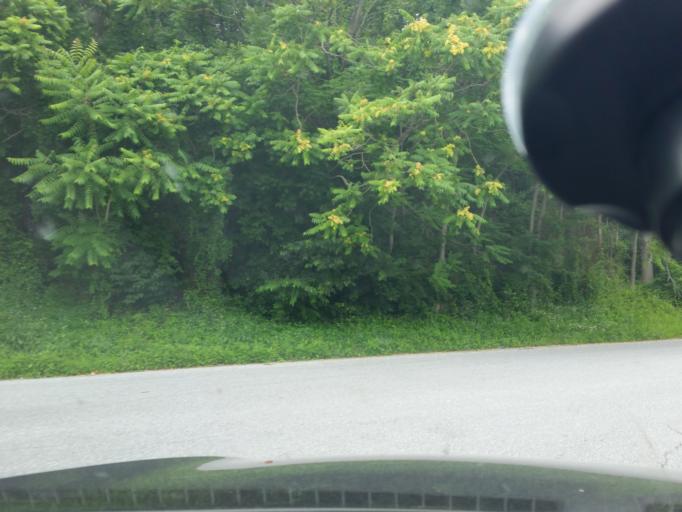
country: US
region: Pennsylvania
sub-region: Cumberland County
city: Enola
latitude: 40.3155
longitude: -76.9303
